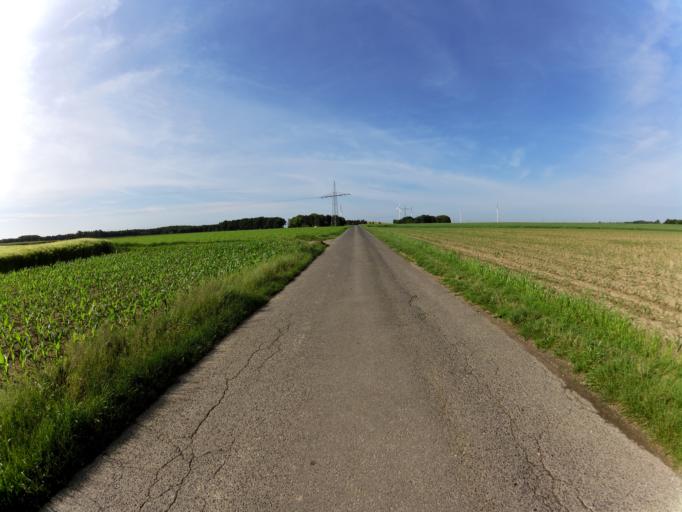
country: DE
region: North Rhine-Westphalia
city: Geilenkirchen
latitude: 51.0021
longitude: 6.0725
